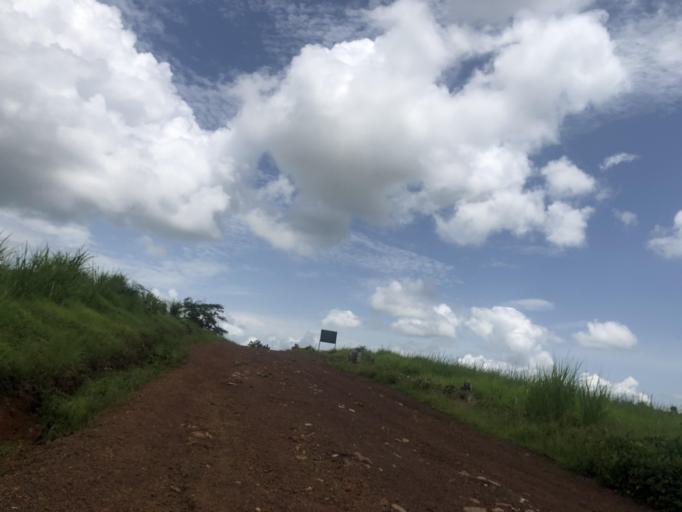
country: SL
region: Northern Province
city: Magburaka
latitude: 8.6902
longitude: -11.9446
